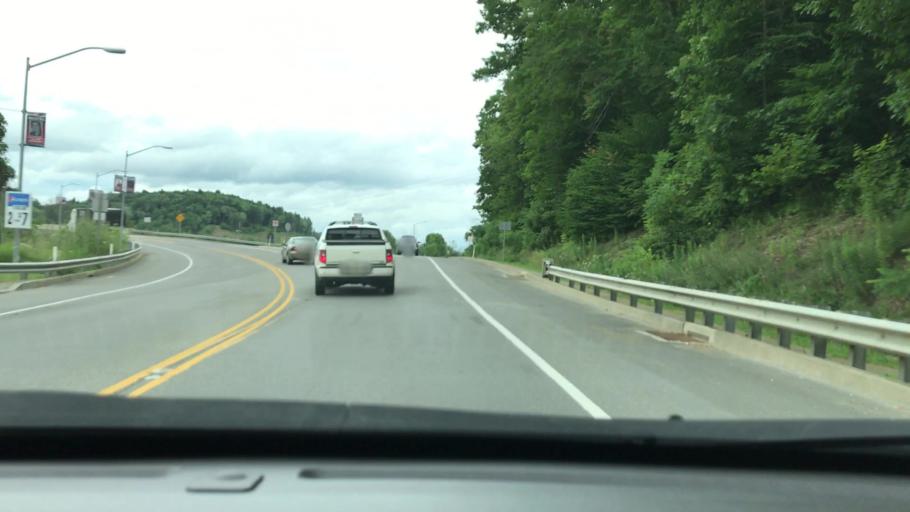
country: US
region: Pennsylvania
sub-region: Elk County
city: Johnsonburg
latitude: 41.4818
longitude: -78.6722
